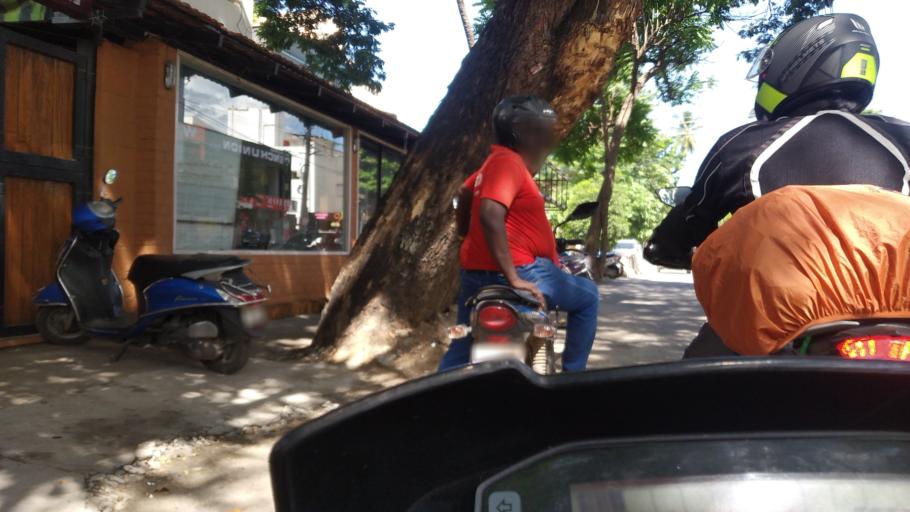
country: IN
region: Tamil Nadu
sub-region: Salem
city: Salem
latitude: 11.6759
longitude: 78.1443
